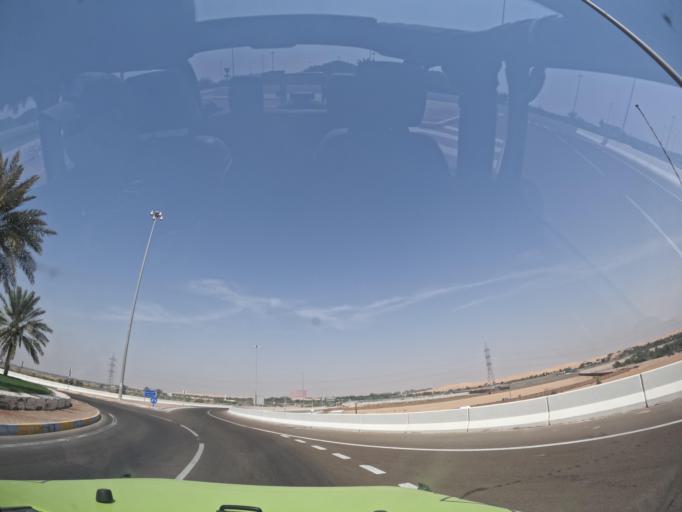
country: AE
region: Abu Dhabi
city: Al Ain
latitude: 24.1774
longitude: 55.1338
